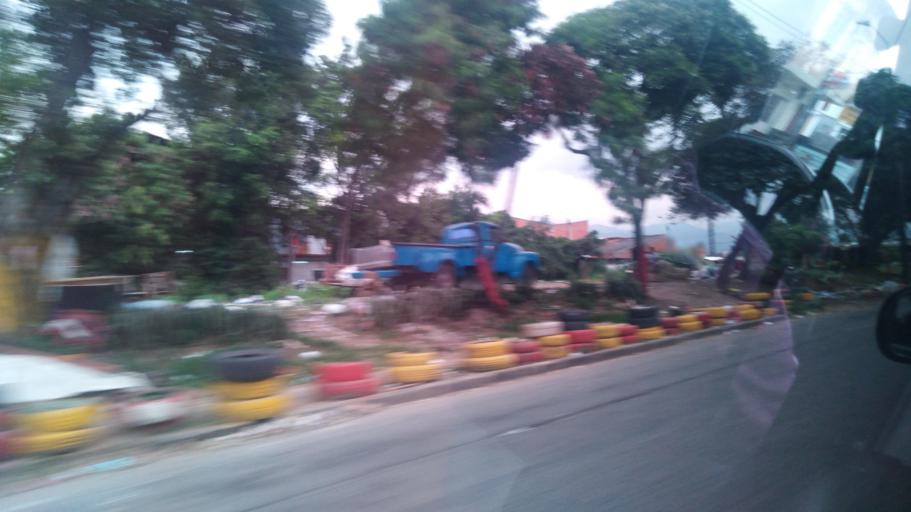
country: CO
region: Valle del Cauca
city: Cali
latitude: 3.4247
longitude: -76.5204
